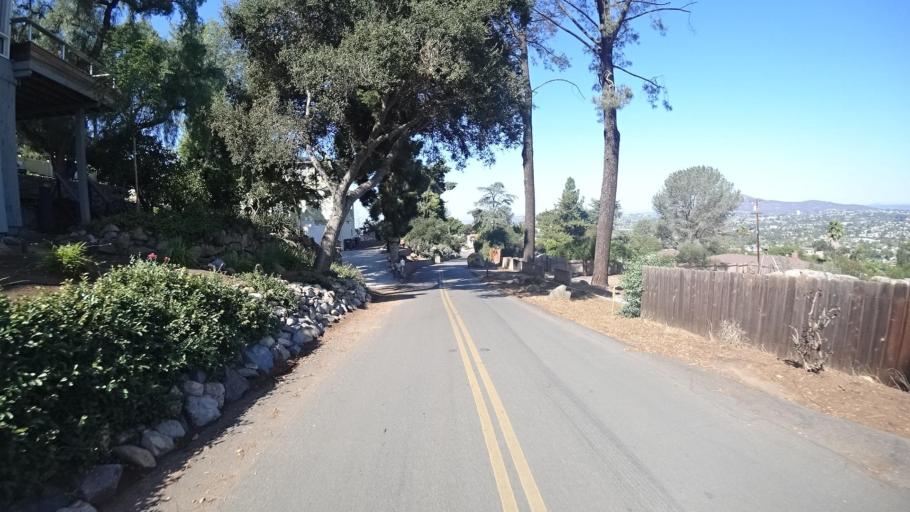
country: US
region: California
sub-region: San Diego County
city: Casa de Oro-Mount Helix
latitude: 32.7753
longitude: -116.9906
